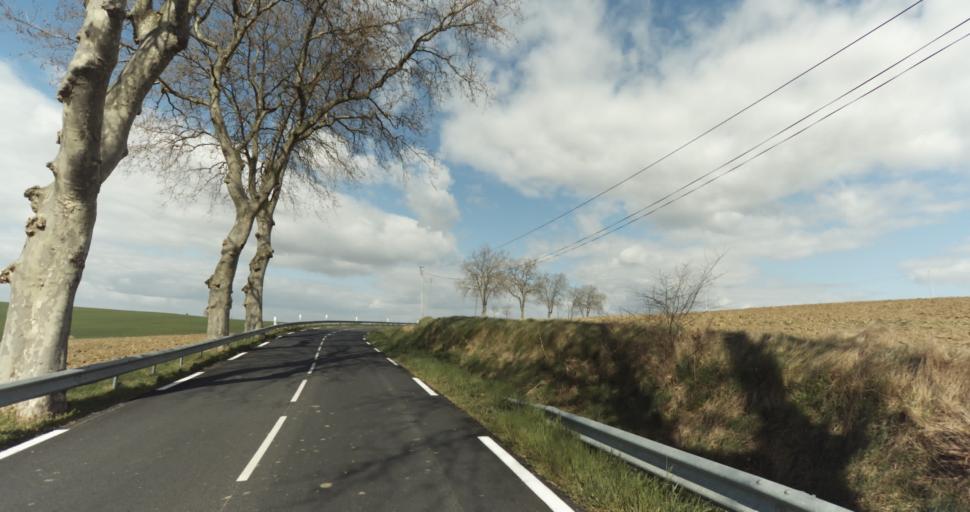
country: FR
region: Midi-Pyrenees
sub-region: Departement de la Haute-Garonne
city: Auterive
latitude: 43.3582
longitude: 1.4958
